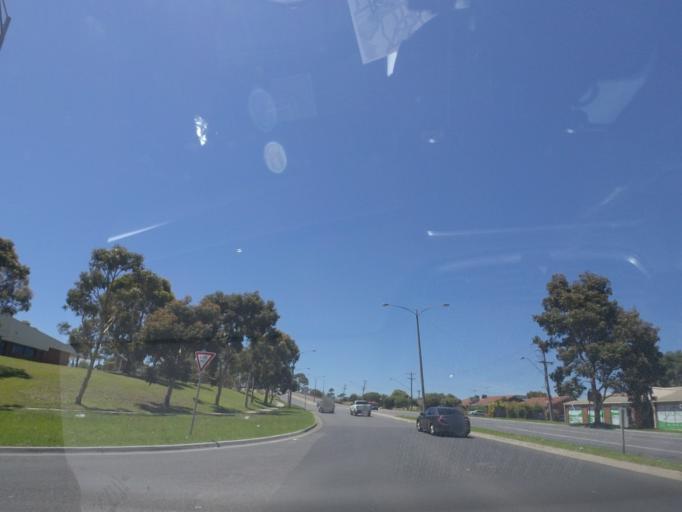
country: AU
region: Victoria
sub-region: Hume
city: Jacana
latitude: -37.6838
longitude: 144.9141
